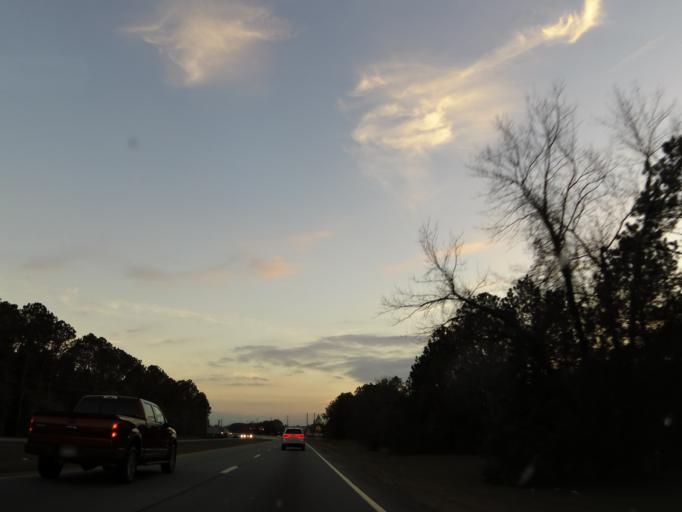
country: US
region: Georgia
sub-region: Dougherty County
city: Albany
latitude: 31.5602
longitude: -84.1144
